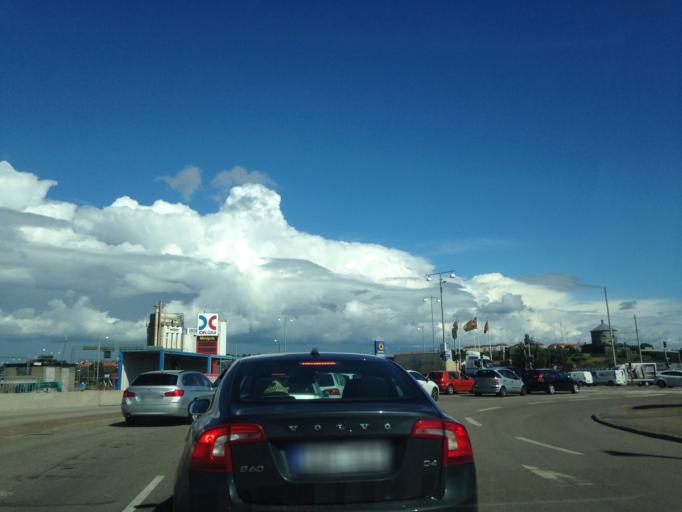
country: SE
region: Vaestra Goetaland
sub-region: Goteborg
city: Goeteborg
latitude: 57.7170
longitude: 11.9814
